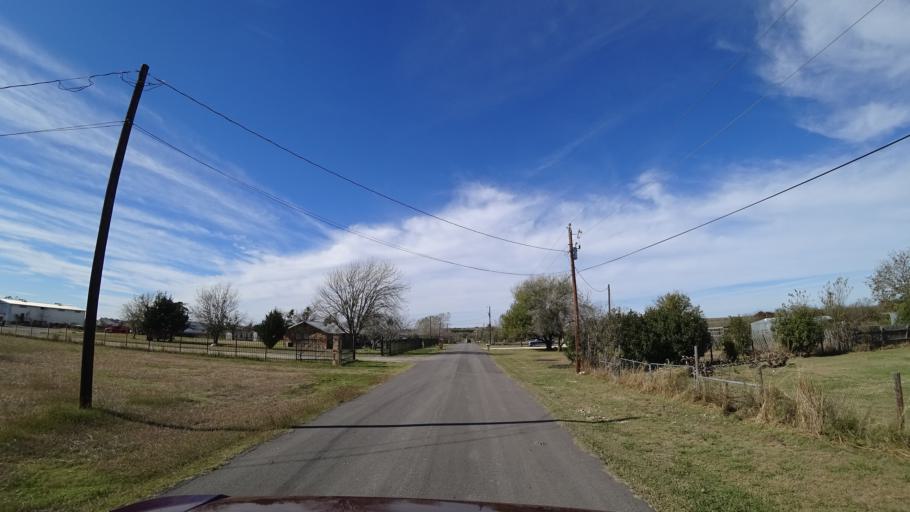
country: US
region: Texas
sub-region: Travis County
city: Onion Creek
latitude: 30.1041
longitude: -97.7176
